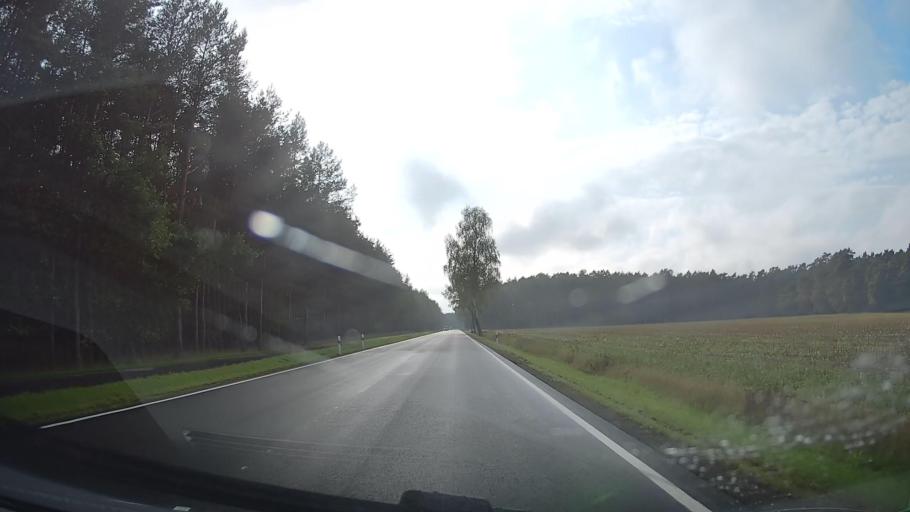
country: DE
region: Mecklenburg-Vorpommern
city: Hagenow
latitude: 53.4717
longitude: 11.2444
